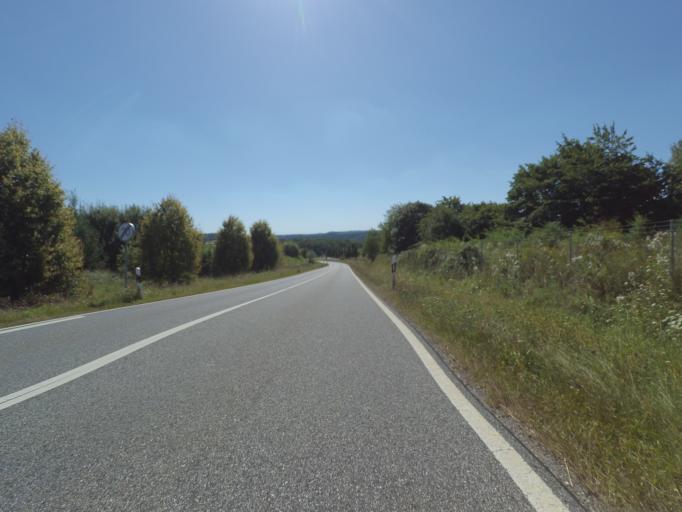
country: DE
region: Rheinland-Pfalz
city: Ulmen
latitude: 50.2092
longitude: 6.9688
